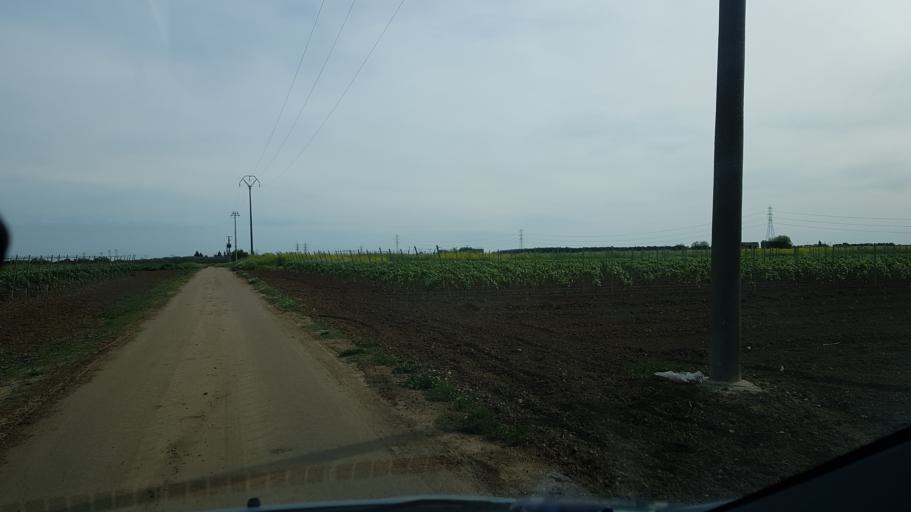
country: IT
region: Apulia
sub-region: Provincia di Brindisi
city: Tuturano
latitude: 40.5722
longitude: 17.9202
